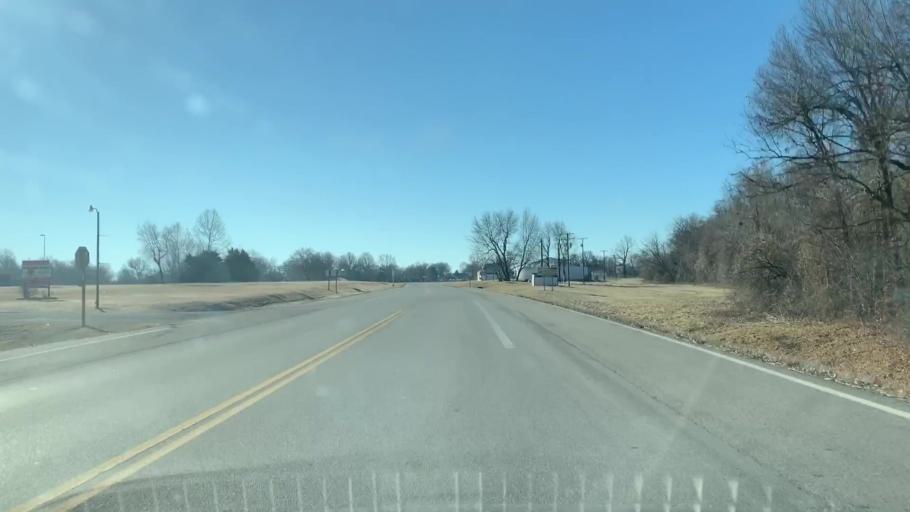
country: US
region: Kansas
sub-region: Cherokee County
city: Baxter Springs
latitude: 37.0380
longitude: -94.7353
